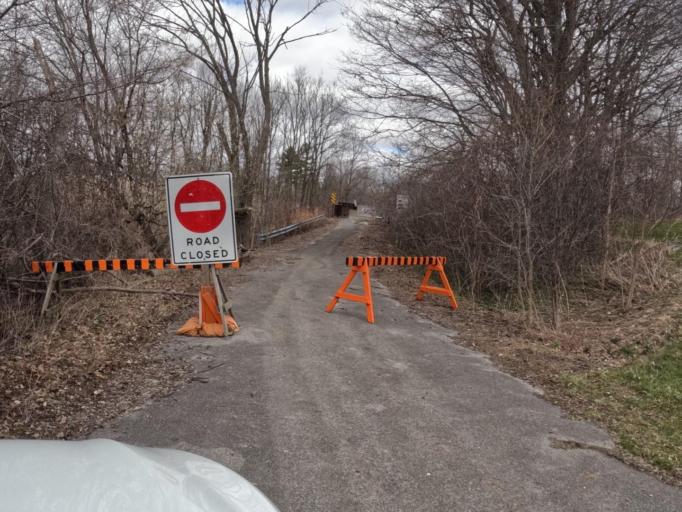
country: CA
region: Ontario
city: Norfolk County
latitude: 42.8239
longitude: -80.1696
